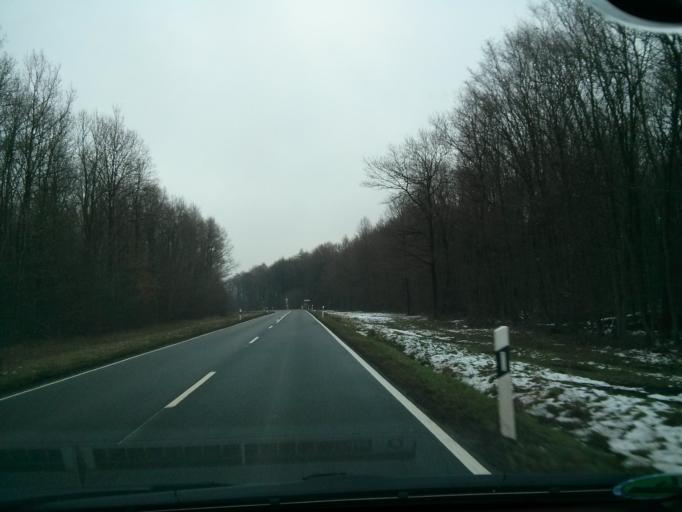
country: DE
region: North Rhine-Westphalia
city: Meckenheim
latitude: 50.6675
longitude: 7.0132
